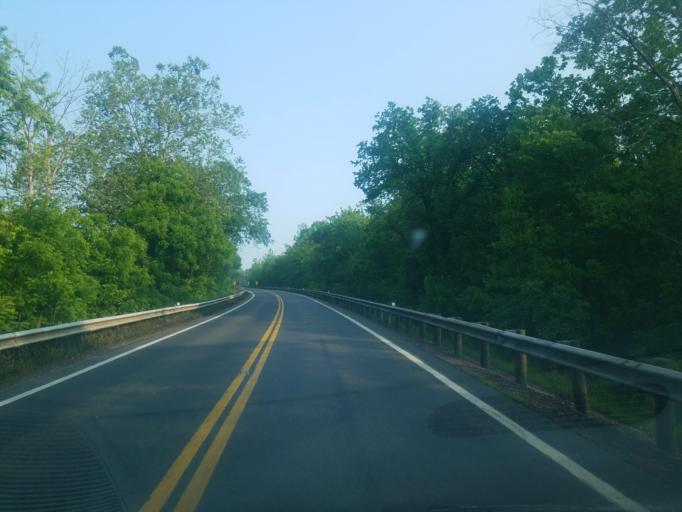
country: US
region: Ohio
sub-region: Tuscarawas County
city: Dover
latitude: 40.5954
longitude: -81.4072
